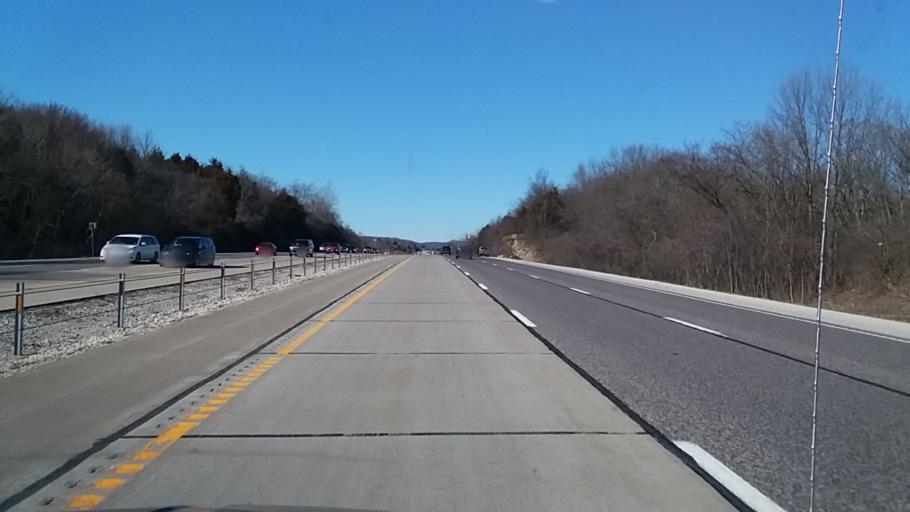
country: US
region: Missouri
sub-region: Jefferson County
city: Pevely
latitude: 38.3097
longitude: -90.4023
